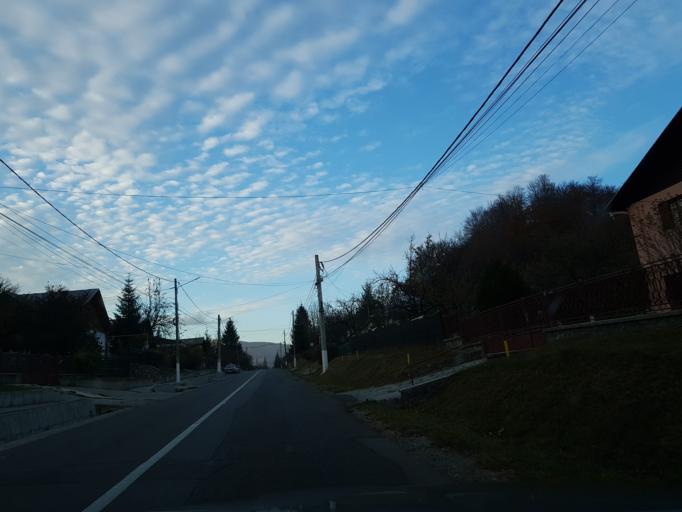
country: RO
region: Prahova
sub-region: Oras Breaza
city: Gura Beliei
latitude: 45.2110
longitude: 25.6463
